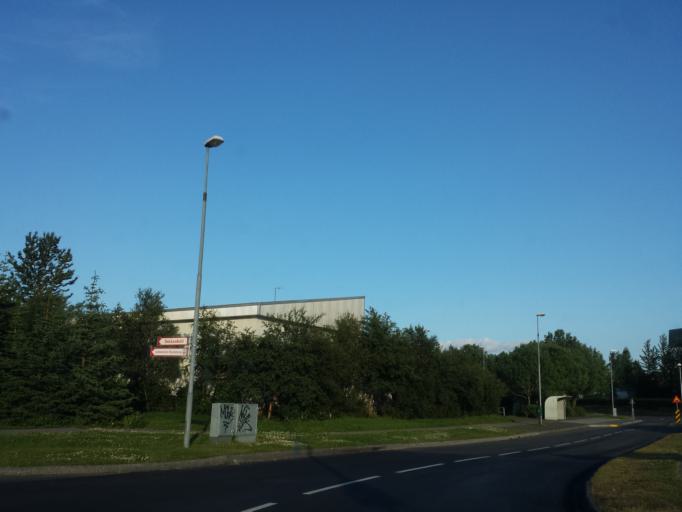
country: IS
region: Capital Region
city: Mosfellsbaer
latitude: 64.1061
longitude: -21.7874
